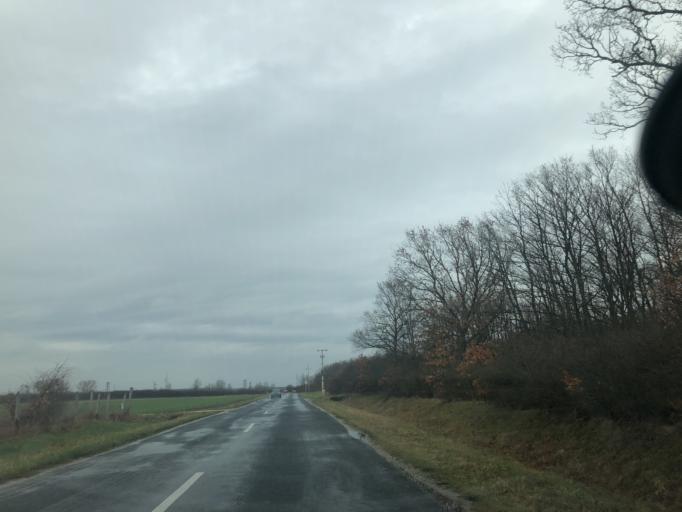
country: HU
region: Gyor-Moson-Sopron
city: Fertoszentmiklos
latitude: 47.5941
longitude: 16.9519
